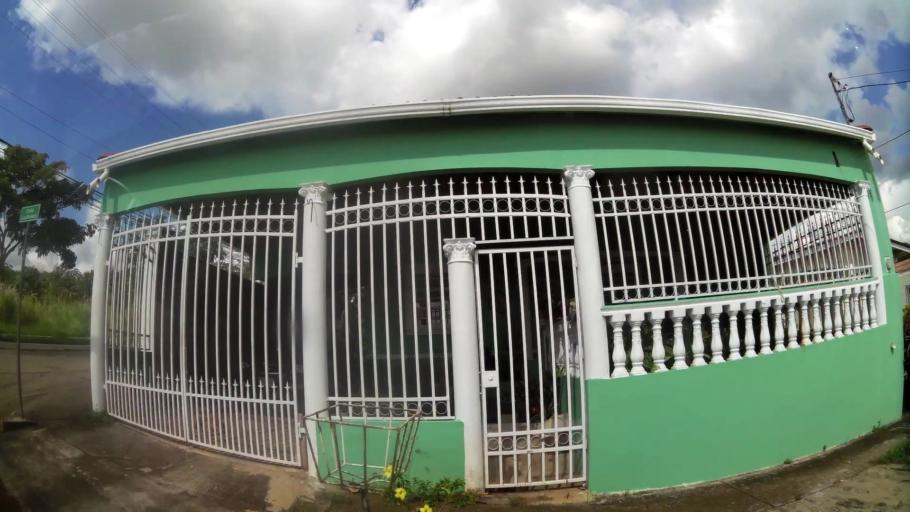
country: PA
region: Panama
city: Nuevo Arraijan
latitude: 8.9180
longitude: -79.7450
